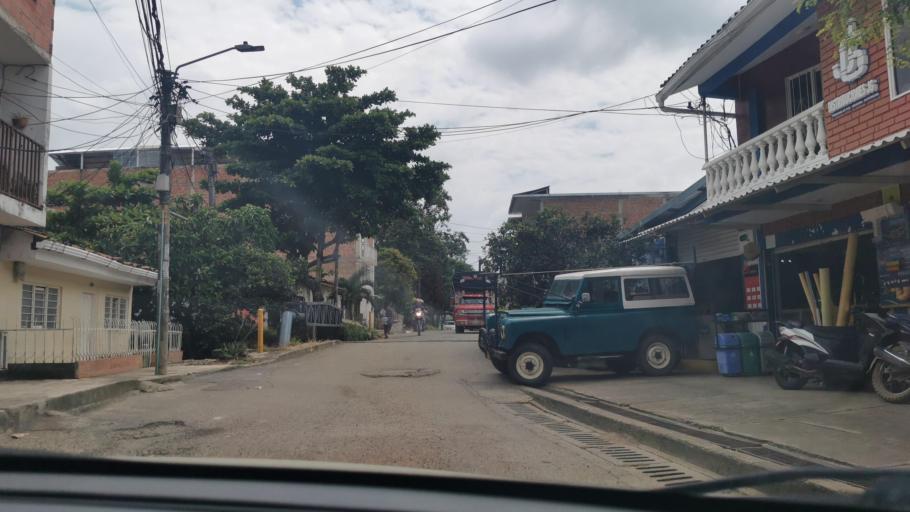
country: CO
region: Valle del Cauca
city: Jamundi
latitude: 3.2645
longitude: -76.5417
